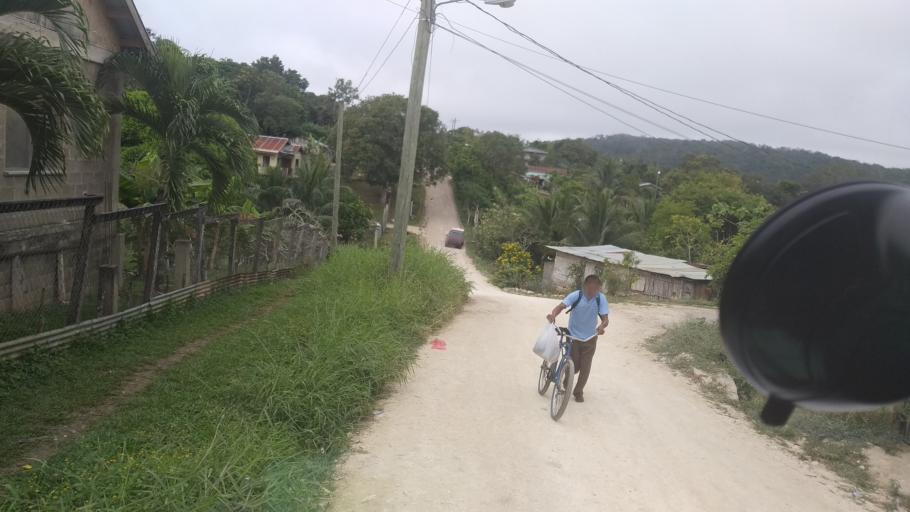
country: BZ
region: Cayo
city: Benque Viejo del Carmen
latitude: 17.0833
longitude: -89.1279
